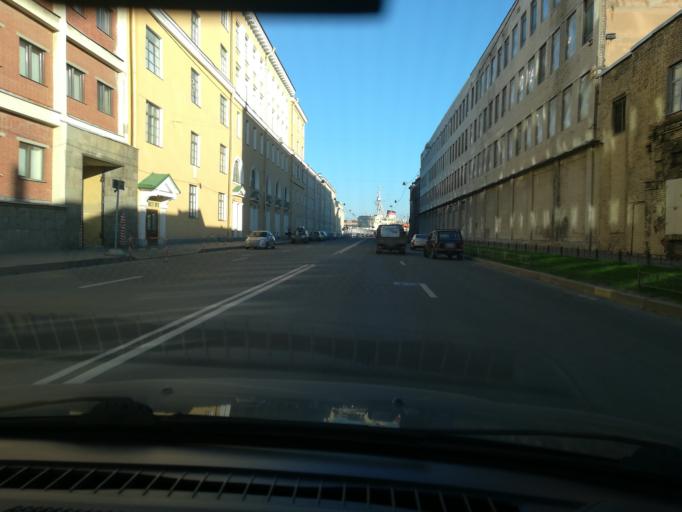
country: RU
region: St.-Petersburg
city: Vasyl'evsky Ostrov
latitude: 59.9305
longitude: 30.2657
